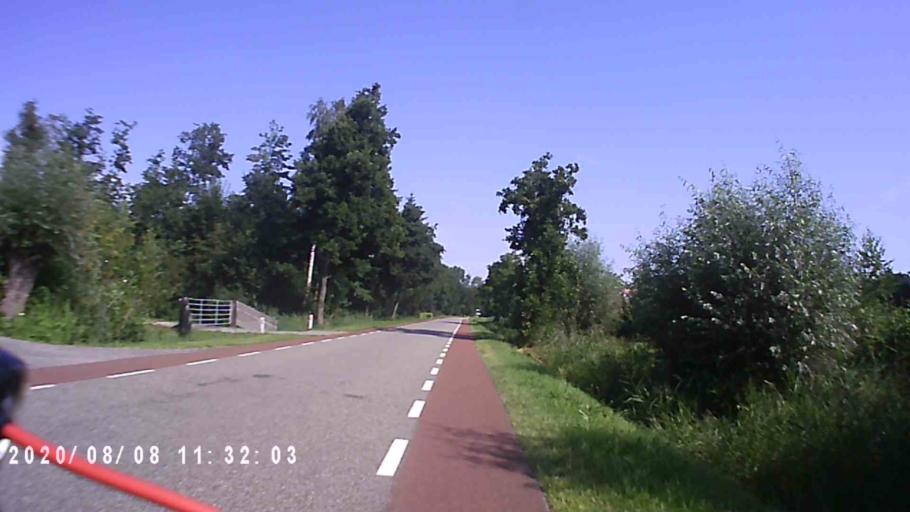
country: NL
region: Groningen
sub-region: Gemeente Zuidhorn
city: Zuidhorn
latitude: 53.2070
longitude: 6.3884
